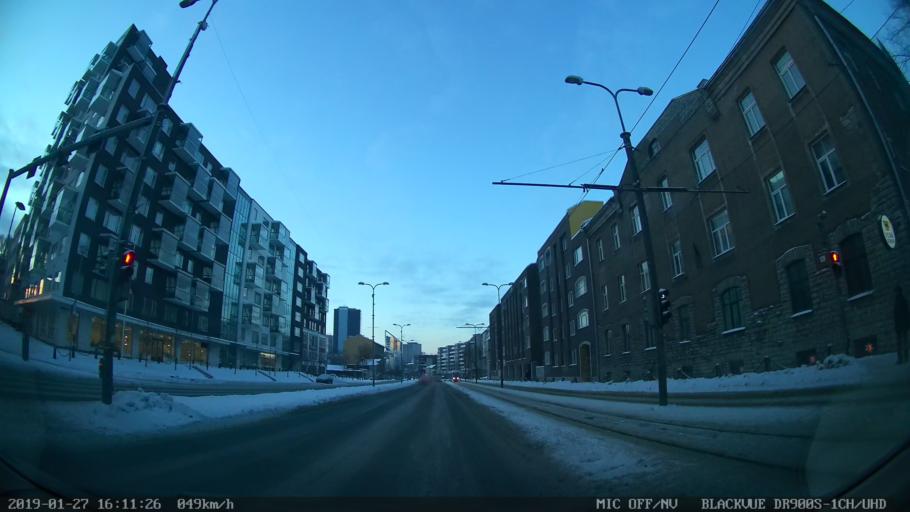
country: EE
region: Harju
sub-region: Tallinna linn
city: Tallinn
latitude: 59.4301
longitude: 24.7719
